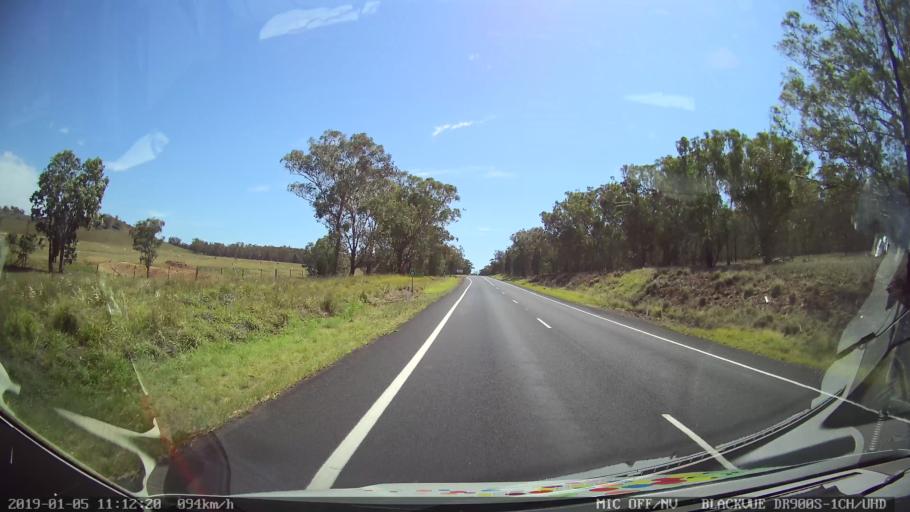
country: AU
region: New South Wales
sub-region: Warrumbungle Shire
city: Coonabarabran
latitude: -31.3830
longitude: 149.2597
